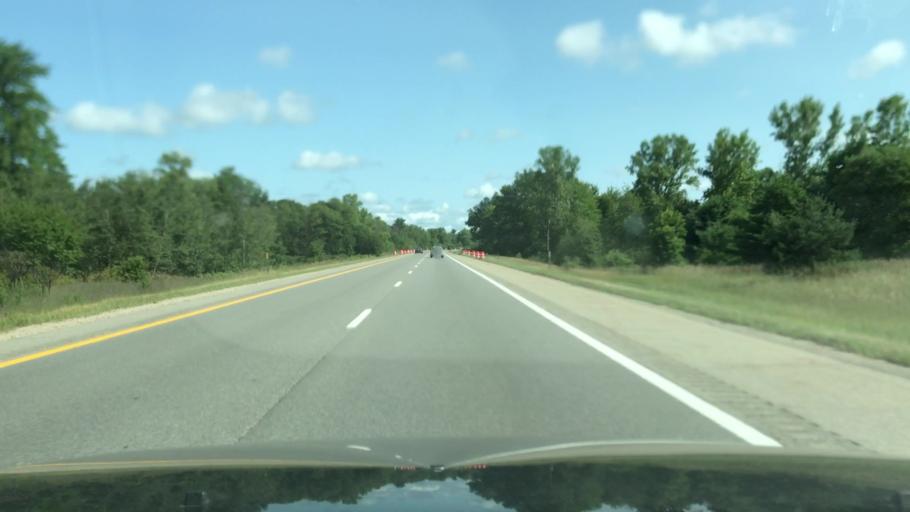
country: US
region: Michigan
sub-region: Kent County
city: Cedar Springs
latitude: 43.2455
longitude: -85.5596
